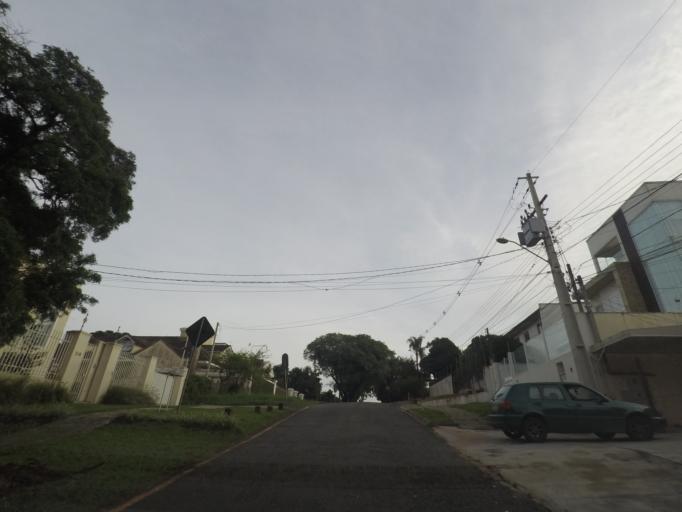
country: BR
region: Parana
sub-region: Curitiba
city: Curitiba
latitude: -25.4265
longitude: -49.3020
